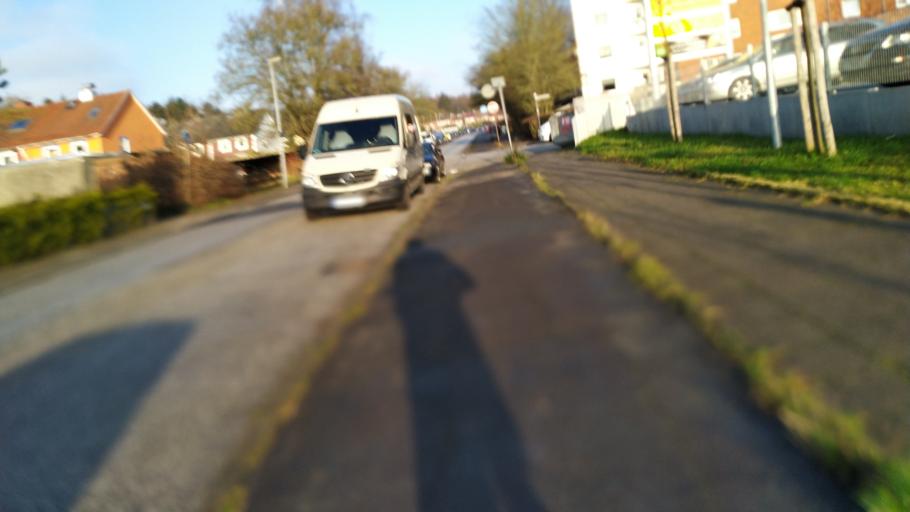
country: DE
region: Mecklenburg-Vorpommern
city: Selmsdorf
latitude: 53.9204
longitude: 10.8152
